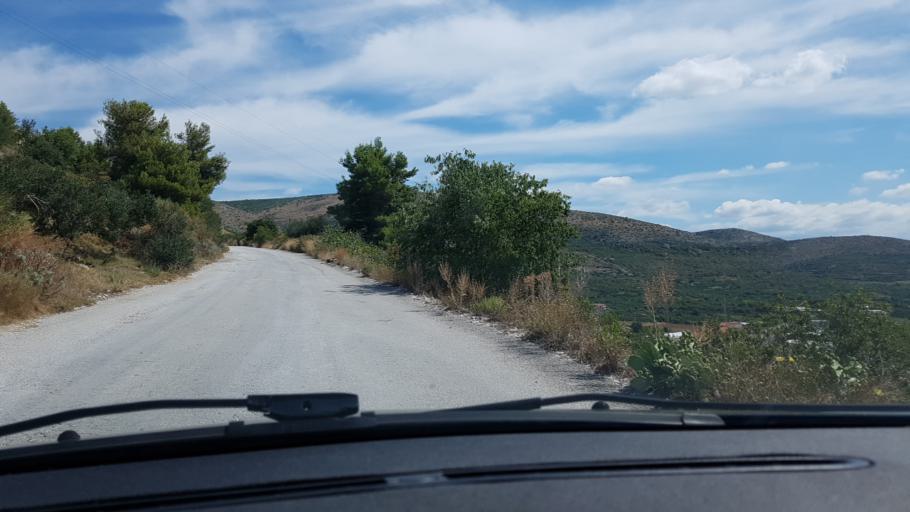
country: HR
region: Splitsko-Dalmatinska
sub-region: Grad Trogir
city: Trogir
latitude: 43.5257
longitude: 16.2278
